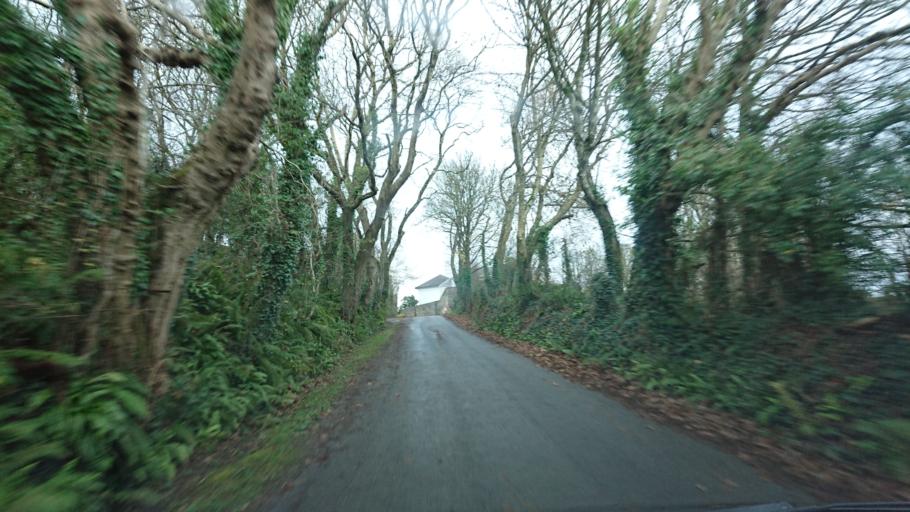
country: IE
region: Munster
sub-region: Waterford
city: Dunmore East
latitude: 52.2006
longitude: -7.0123
